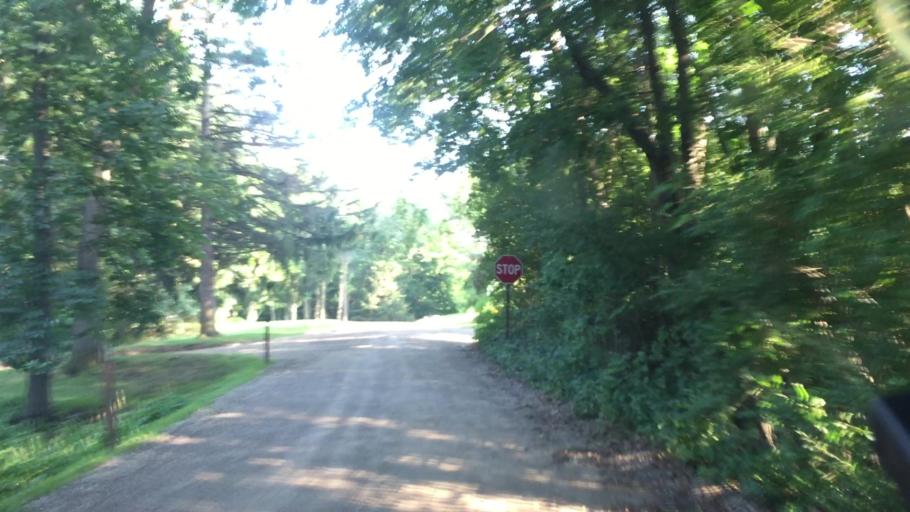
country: US
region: Michigan
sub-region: Oakland County
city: Bloomfield Hills
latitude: 42.5652
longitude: -83.2733
